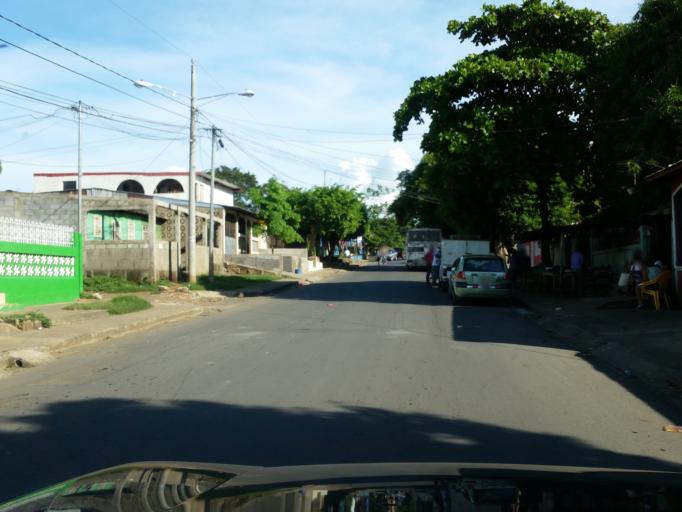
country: NI
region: Managua
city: Managua
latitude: 12.1152
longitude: -86.2323
